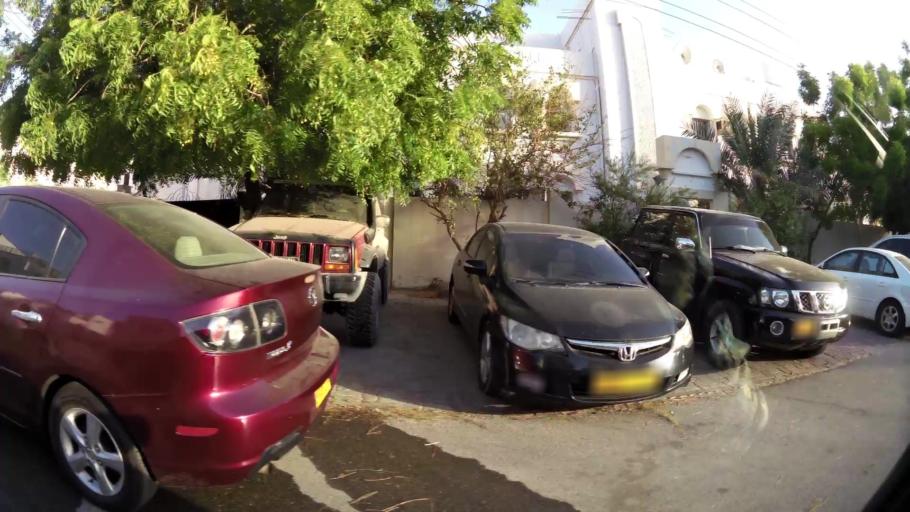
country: OM
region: Muhafazat Masqat
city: Muscat
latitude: 23.5675
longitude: 58.5797
